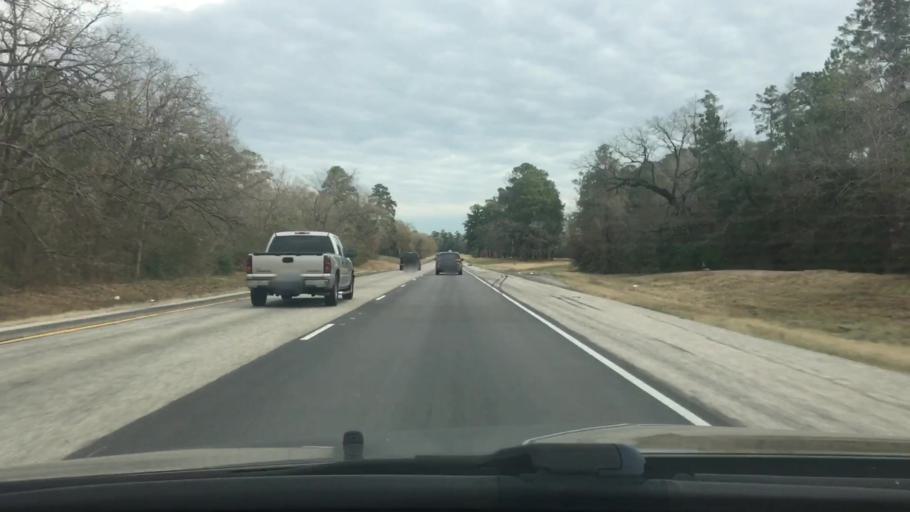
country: US
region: Texas
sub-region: Walker County
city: Huntsville
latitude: 30.8009
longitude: -95.6843
